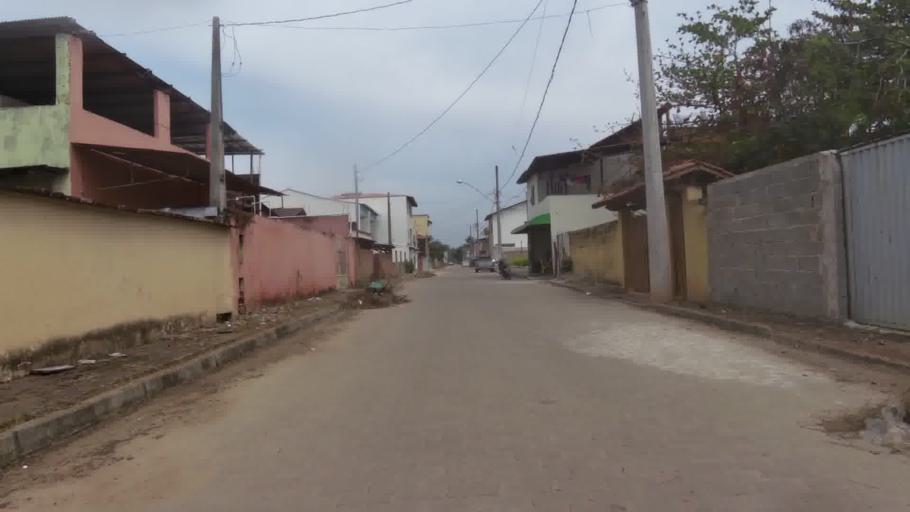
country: BR
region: Espirito Santo
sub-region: Piuma
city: Piuma
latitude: -20.8445
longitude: -40.7477
